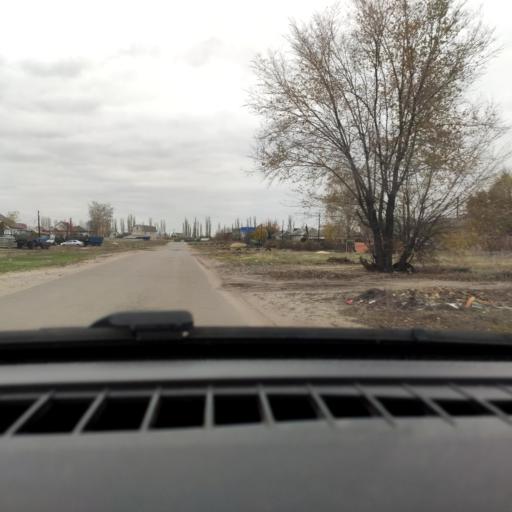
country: RU
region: Voronezj
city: Maslovka
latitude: 51.5795
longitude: 39.3029
